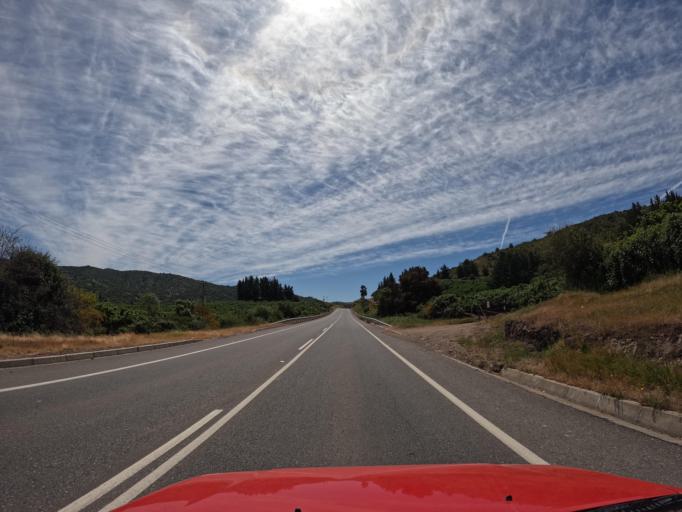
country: CL
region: Maule
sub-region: Provincia de Talca
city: Talca
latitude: -35.2603
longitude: -71.5425
